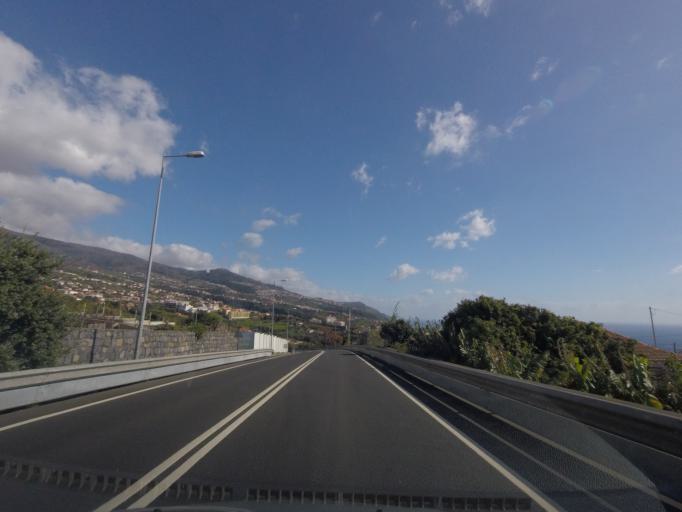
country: PT
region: Madeira
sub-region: Calheta
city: Estreito da Calheta
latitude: 32.7305
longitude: -17.1887
